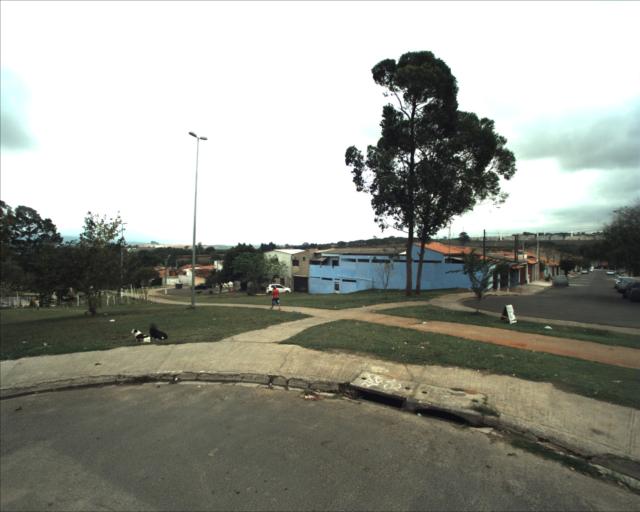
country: BR
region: Sao Paulo
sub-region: Sorocaba
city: Sorocaba
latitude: -23.4312
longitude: -47.5120
